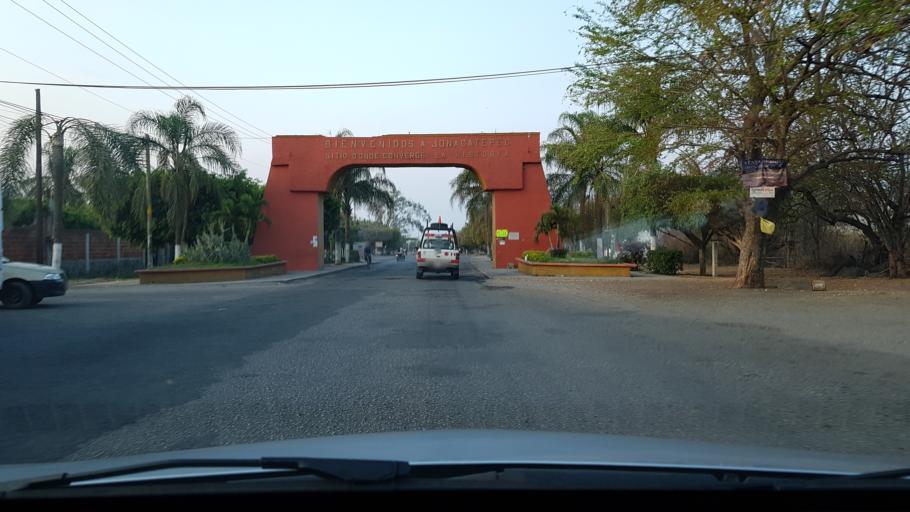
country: MX
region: Morelos
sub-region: Jonacatepec
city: Amacuitlapilco
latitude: 18.7007
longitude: -98.8012
